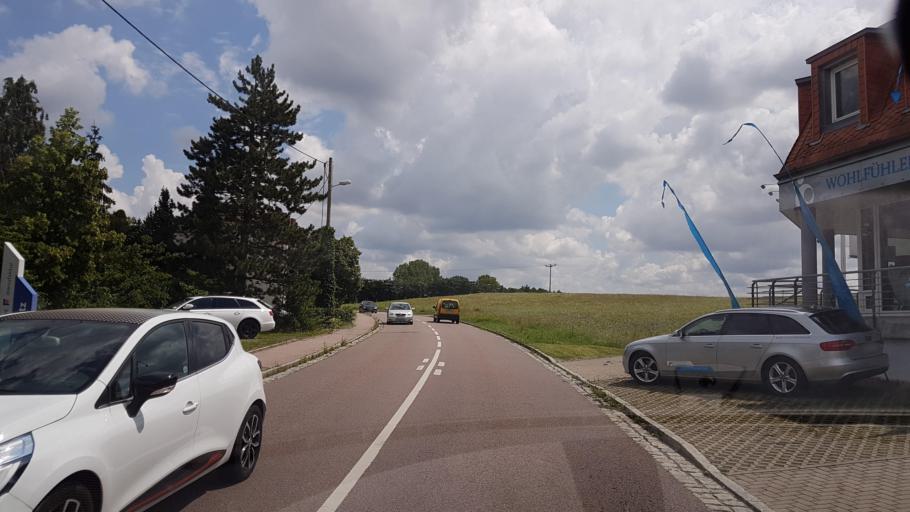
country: DE
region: Saxony
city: Nunchritz
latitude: 51.2832
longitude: 13.4041
